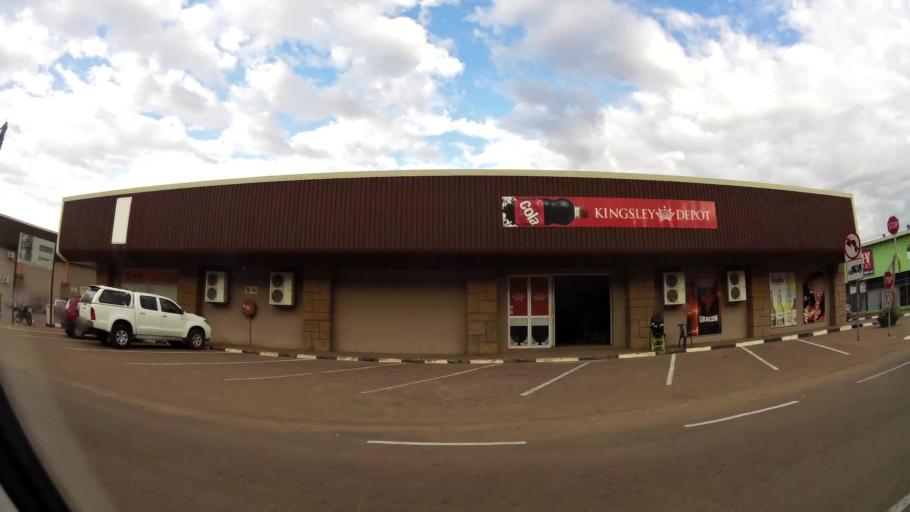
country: ZA
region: Limpopo
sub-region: Waterberg District Municipality
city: Modimolle
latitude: -24.5215
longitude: 28.7104
